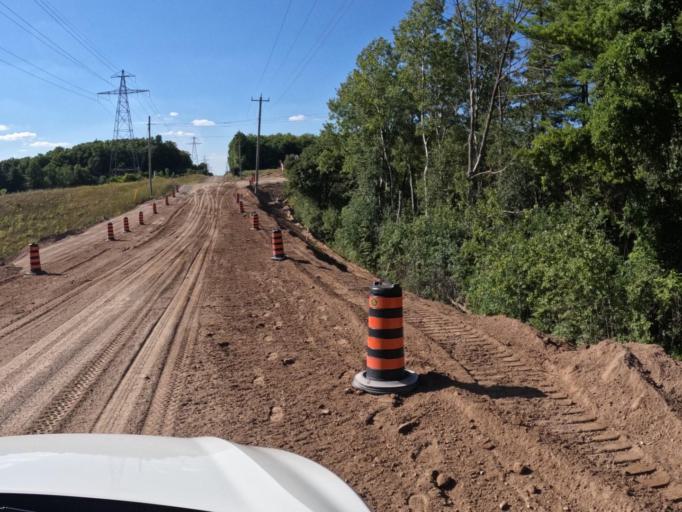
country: CA
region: Ontario
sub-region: Wellington County
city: Guelph
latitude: 43.4341
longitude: -80.1349
